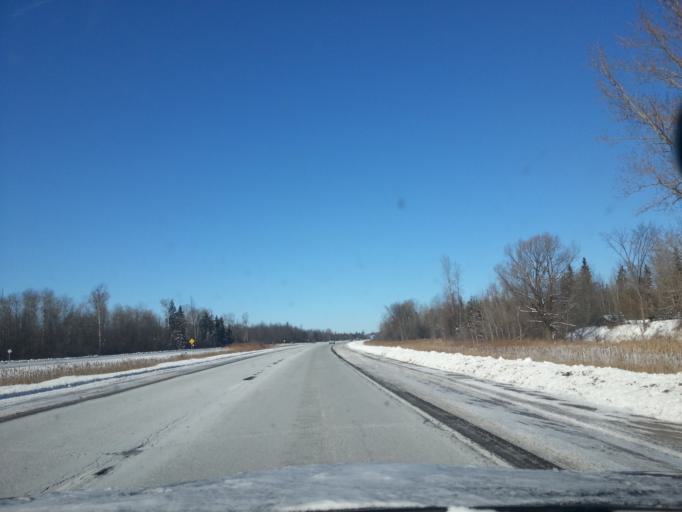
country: CA
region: Ontario
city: Bells Corners
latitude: 45.2978
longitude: -76.0243
